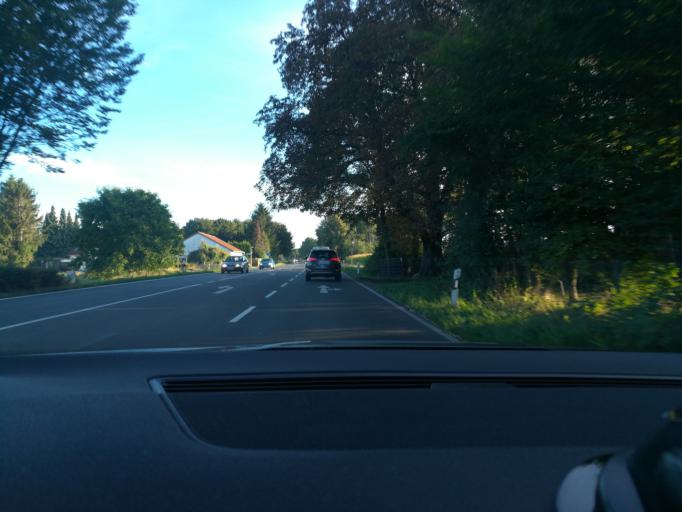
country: DE
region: North Rhine-Westphalia
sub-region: Regierungsbezirk Detmold
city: Minden
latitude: 52.3204
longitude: 8.8804
